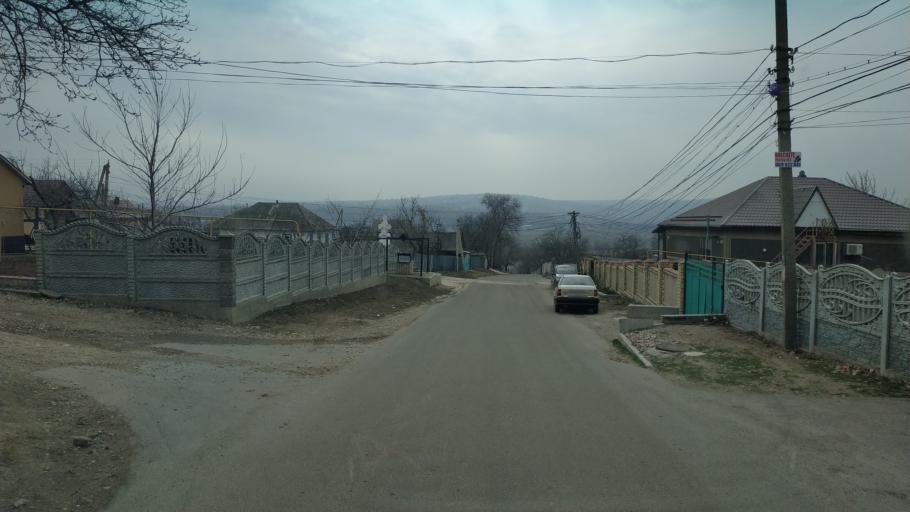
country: MD
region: Chisinau
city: Singera
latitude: 46.9356
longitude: 28.9848
